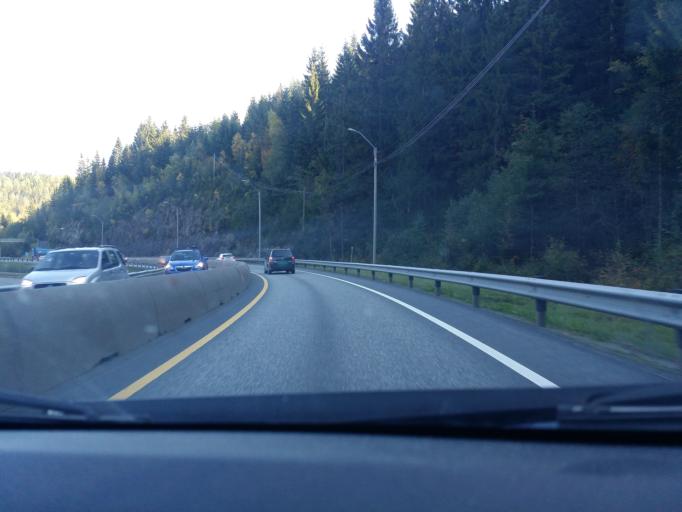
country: NO
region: Akershus
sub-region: Baerum
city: Skui
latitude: 59.9468
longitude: 10.3898
